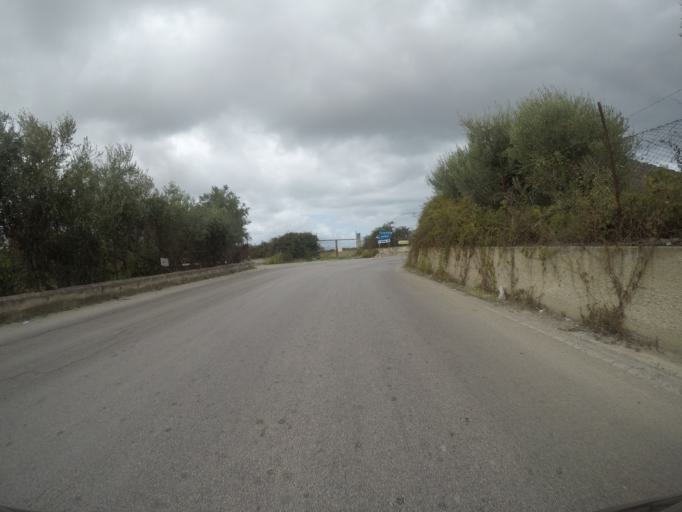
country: IT
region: Sicily
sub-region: Palermo
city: Partinico
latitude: 38.0865
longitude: 13.1109
